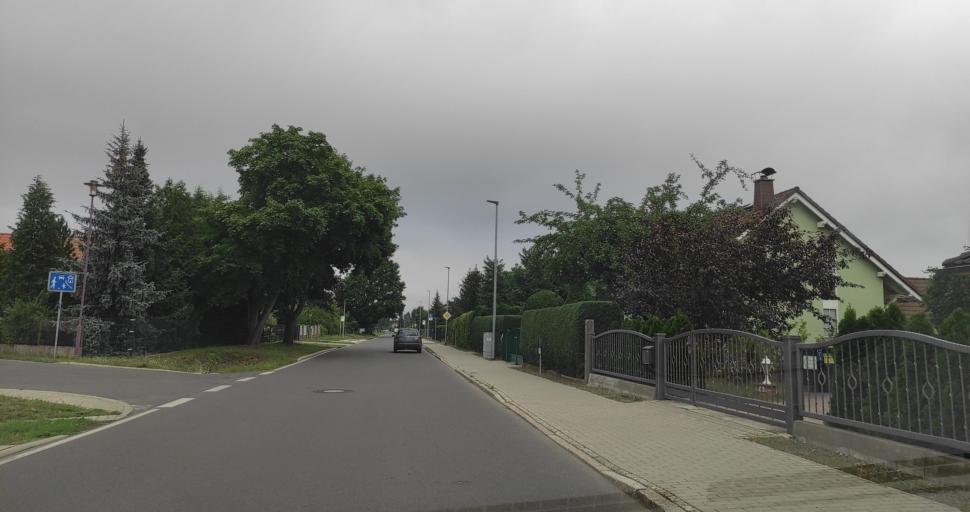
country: DE
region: Brandenburg
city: Forst
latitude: 51.7209
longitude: 14.6362
